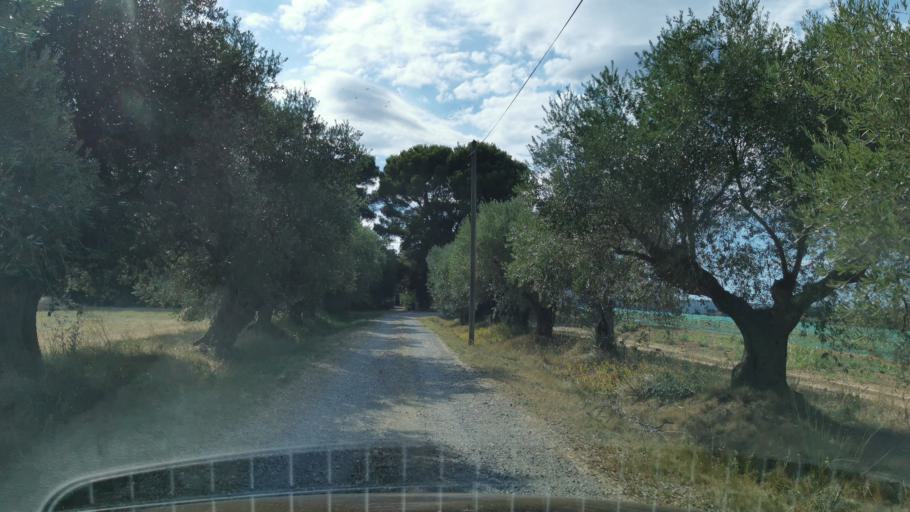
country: FR
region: Languedoc-Roussillon
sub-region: Departement de l'Aude
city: Ginestas
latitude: 43.2854
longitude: 2.8657
